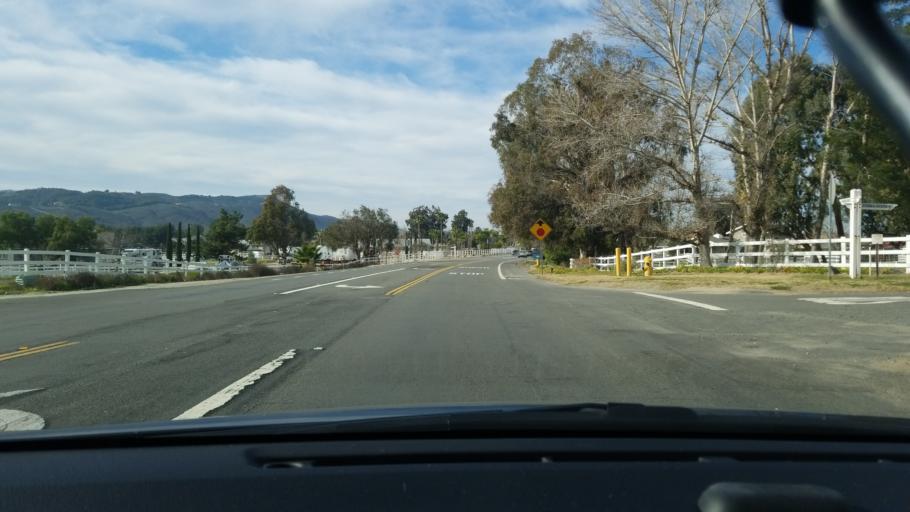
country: US
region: California
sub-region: Riverside County
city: Temecula
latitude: 33.4804
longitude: -117.1309
